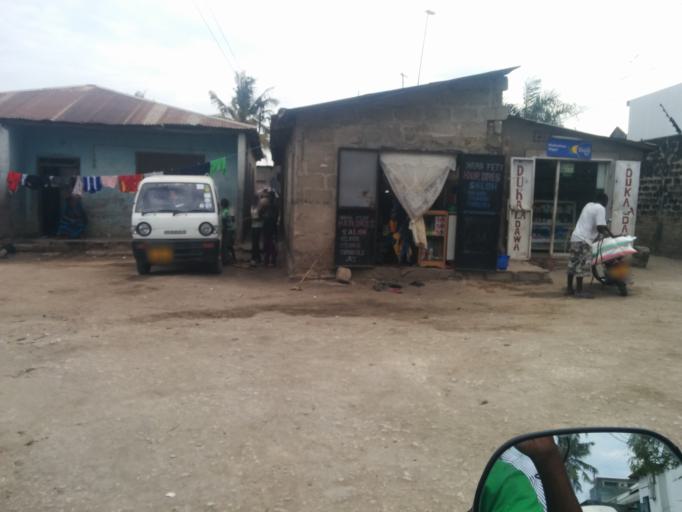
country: TZ
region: Dar es Salaam
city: Dar es Salaam
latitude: -6.8346
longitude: 39.2743
